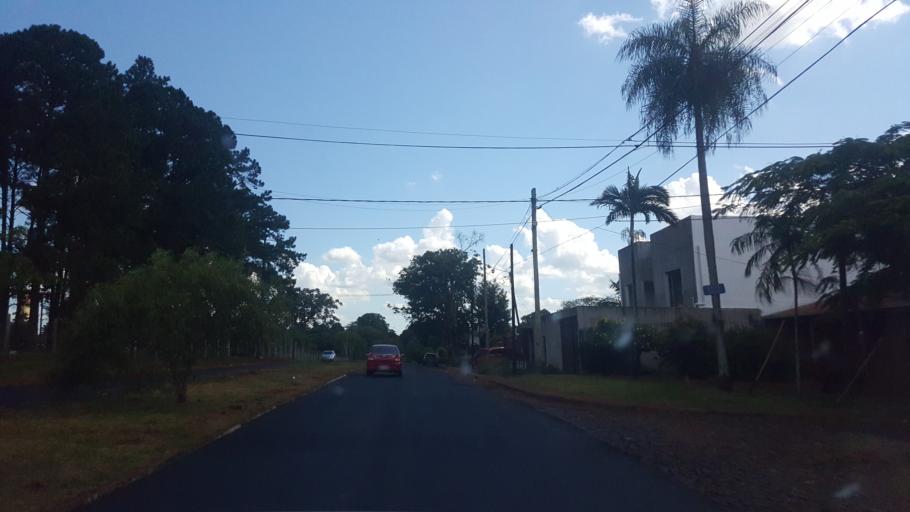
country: AR
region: Misiones
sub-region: Departamento de Capital
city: Posadas
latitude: -27.3592
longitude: -55.9193
